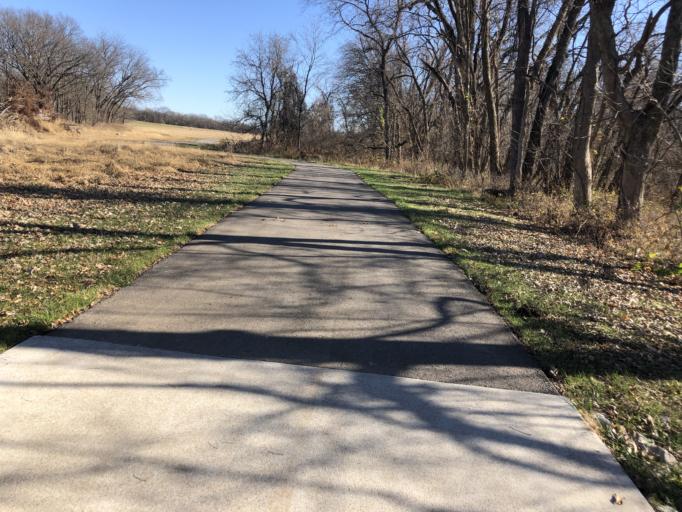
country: US
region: Kansas
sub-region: Johnson County
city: Gardner
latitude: 38.8790
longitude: -94.9669
